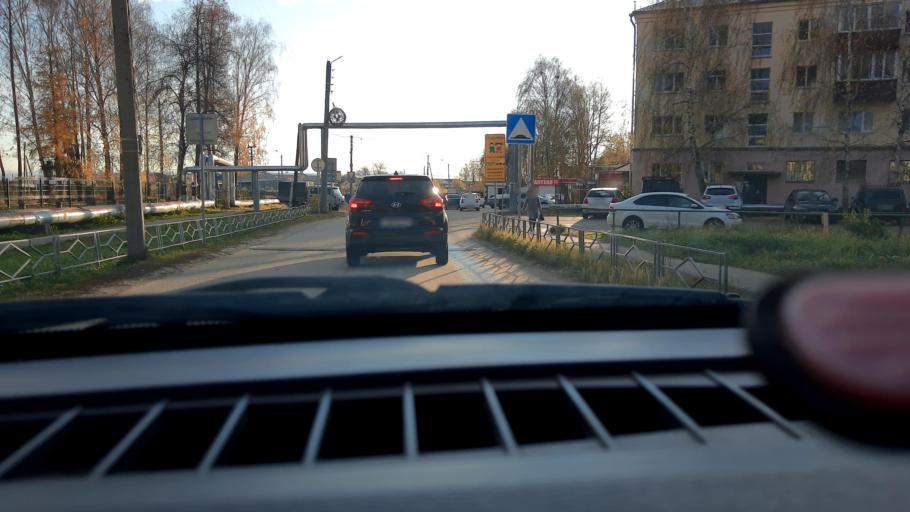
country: RU
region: Nizjnij Novgorod
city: Afonino
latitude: 56.2100
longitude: 44.1010
